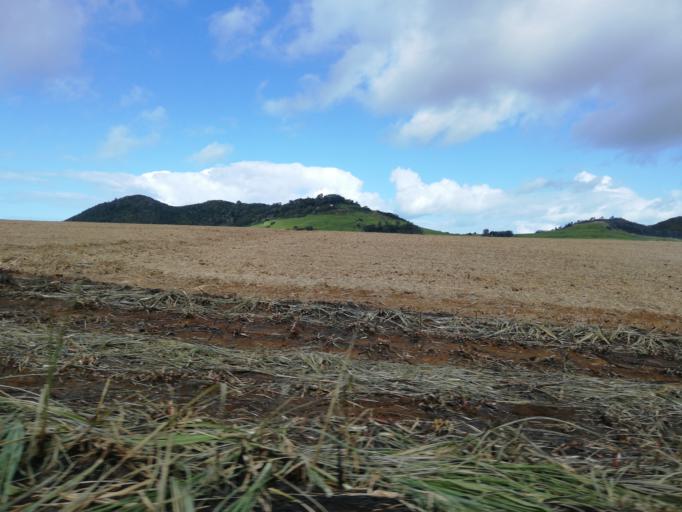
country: MU
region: Flacq
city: Grande Riviere Sud Est
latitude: -20.2844
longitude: 57.7547
